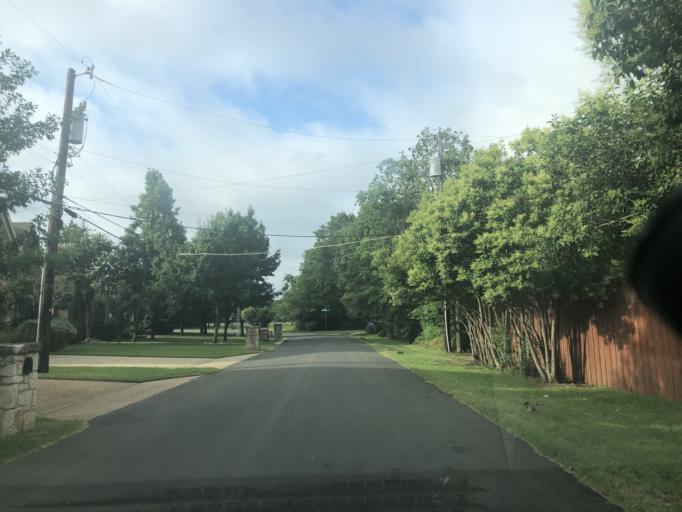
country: US
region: Texas
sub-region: Dallas County
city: University Park
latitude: 32.8528
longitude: -96.8409
